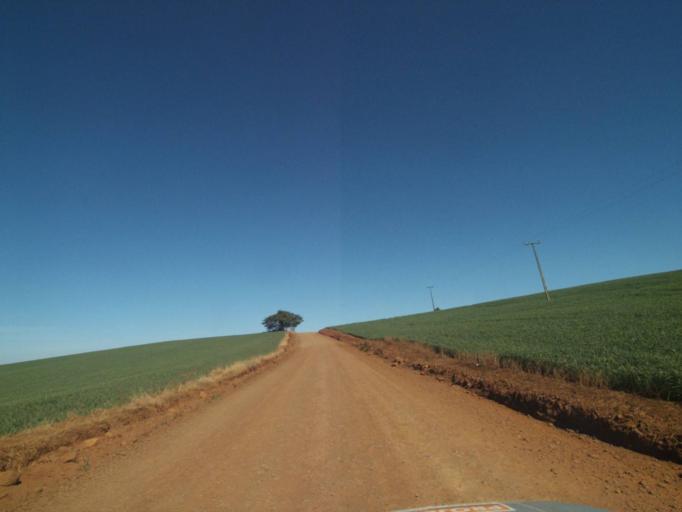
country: BR
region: Parana
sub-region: Tibagi
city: Tibagi
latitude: -24.6028
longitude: -50.6034
